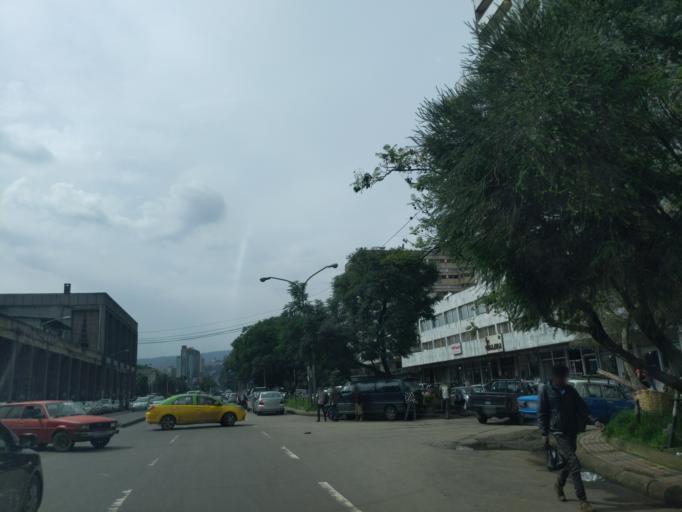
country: ET
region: Adis Abeba
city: Addis Ababa
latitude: 9.0153
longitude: 38.7528
